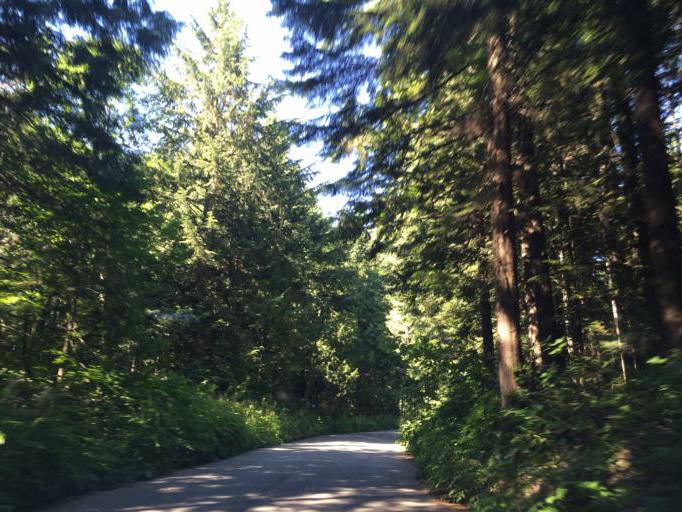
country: US
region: Washington
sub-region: King County
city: Tanner
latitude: 47.4037
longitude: -121.4451
